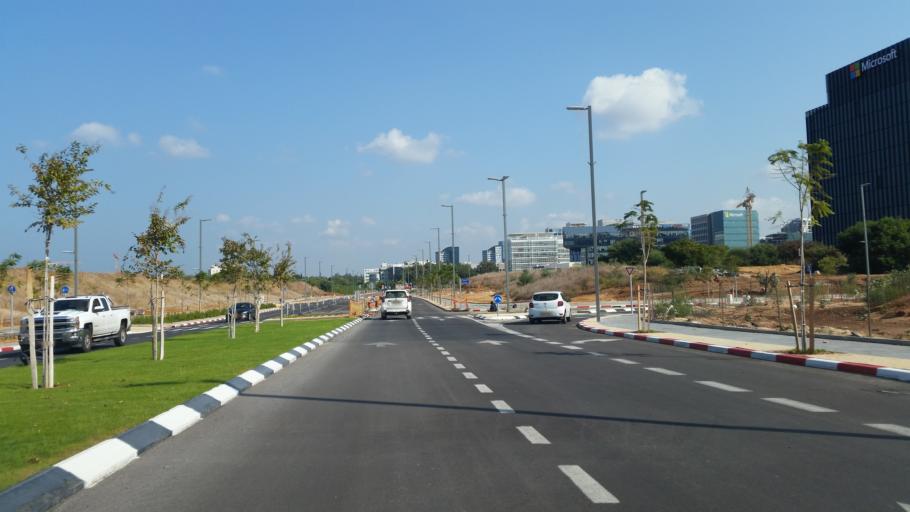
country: IL
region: Tel Aviv
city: Herzliya Pituah
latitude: 32.1565
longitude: 34.8029
